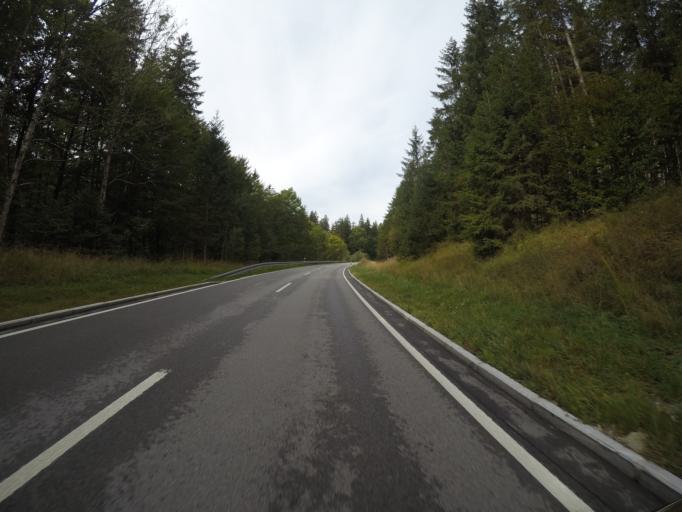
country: AT
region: Tyrol
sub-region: Politischer Bezirk Schwaz
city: Achenkirch
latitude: 47.5812
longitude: 11.6124
